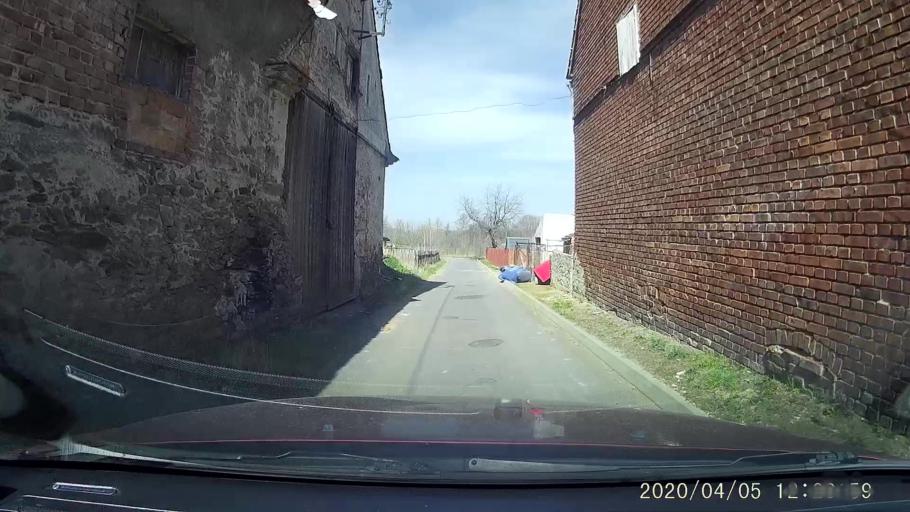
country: PL
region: Lower Silesian Voivodeship
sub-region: Powiat lubanski
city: Olszyna
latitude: 51.0153
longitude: 15.3411
